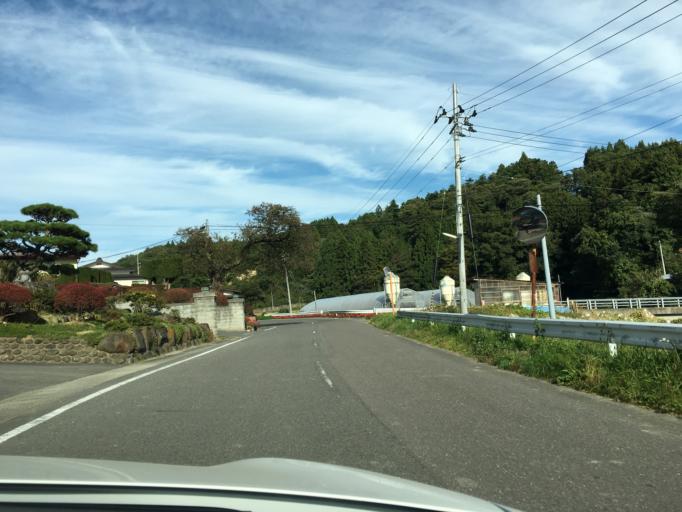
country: JP
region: Fukushima
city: Miharu
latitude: 37.3339
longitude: 140.5013
